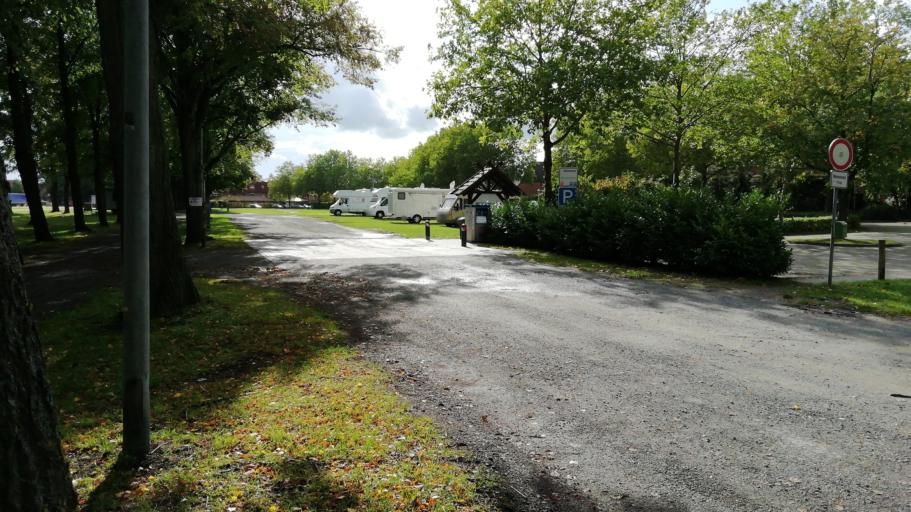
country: DE
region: Lower Saxony
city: Diepholz
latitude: 52.6131
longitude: 8.3708
